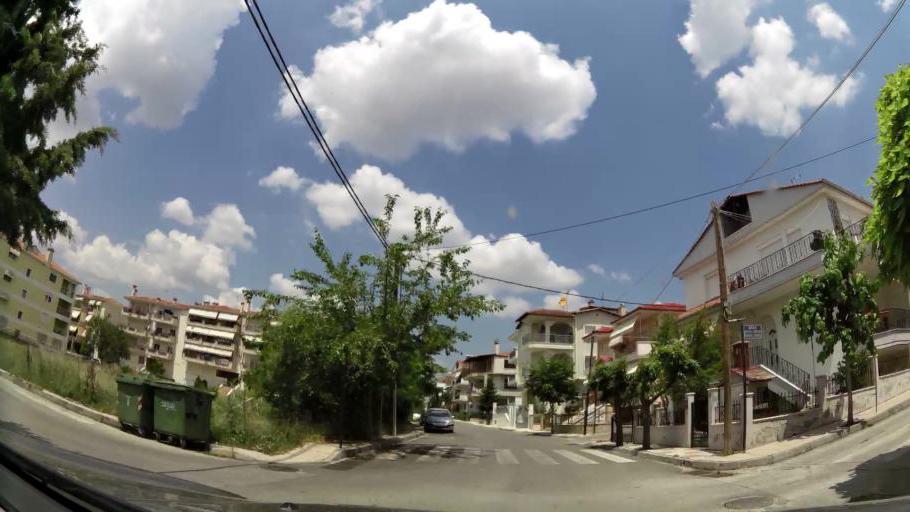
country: GR
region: West Macedonia
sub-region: Nomos Kozanis
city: Kozani
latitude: 40.2909
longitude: 21.7966
